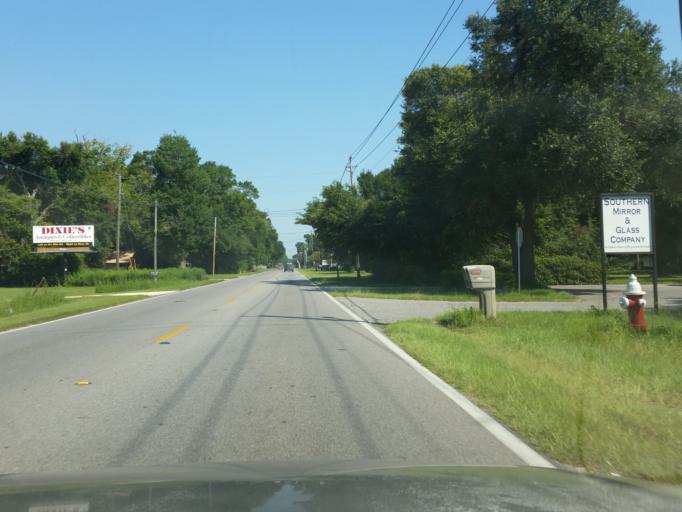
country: US
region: Florida
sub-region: Escambia County
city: Ensley
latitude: 30.5386
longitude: -87.2766
